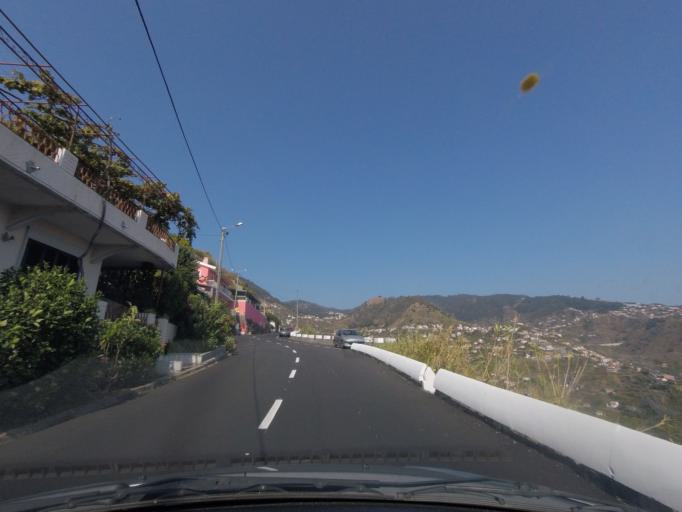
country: PT
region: Madeira
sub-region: Ribeira Brava
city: Campanario
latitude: 32.6664
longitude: -17.0487
